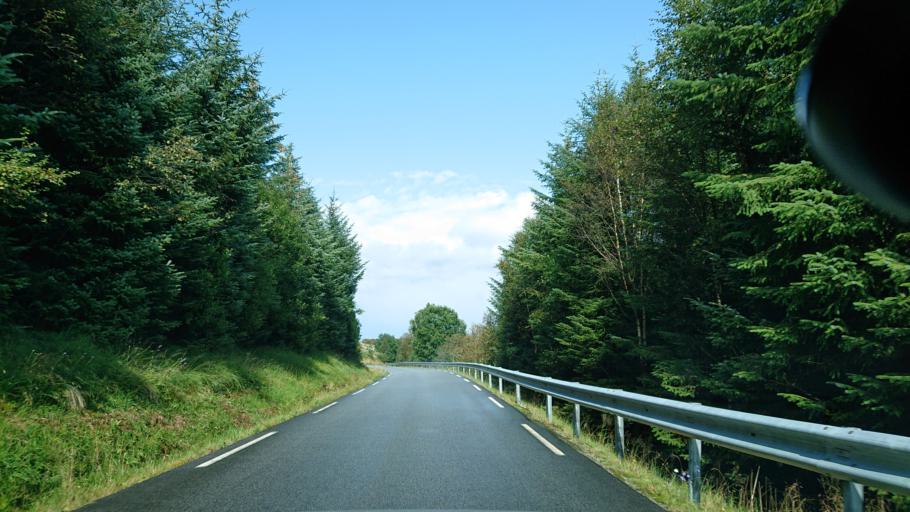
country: NO
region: Rogaland
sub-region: Gjesdal
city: Algard
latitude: 58.6893
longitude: 5.8758
